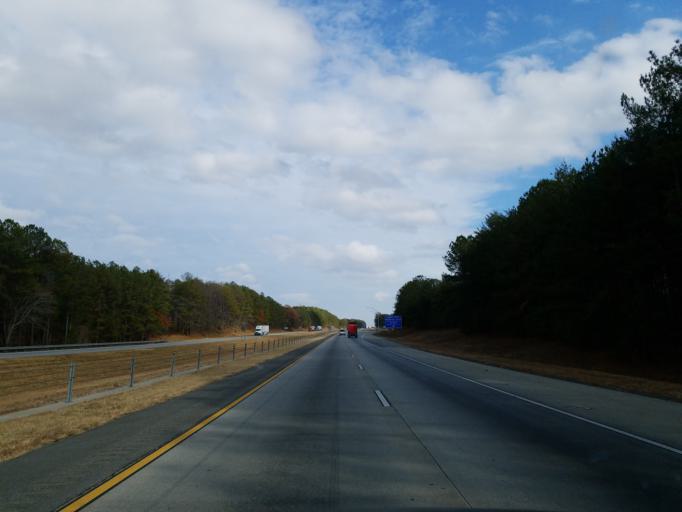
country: US
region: Georgia
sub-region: Haralson County
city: Tallapoosa
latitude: 33.6779
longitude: -85.3278
